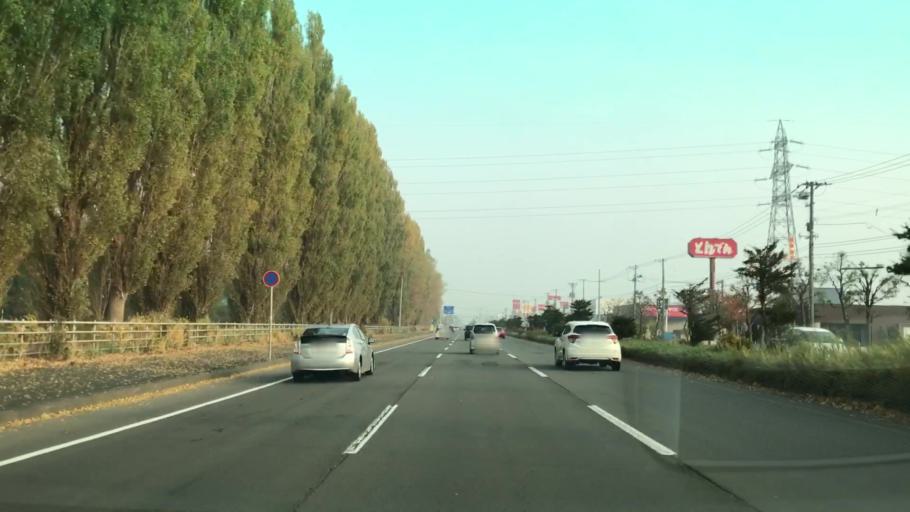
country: JP
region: Hokkaido
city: Sapporo
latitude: 43.1418
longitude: 141.3489
